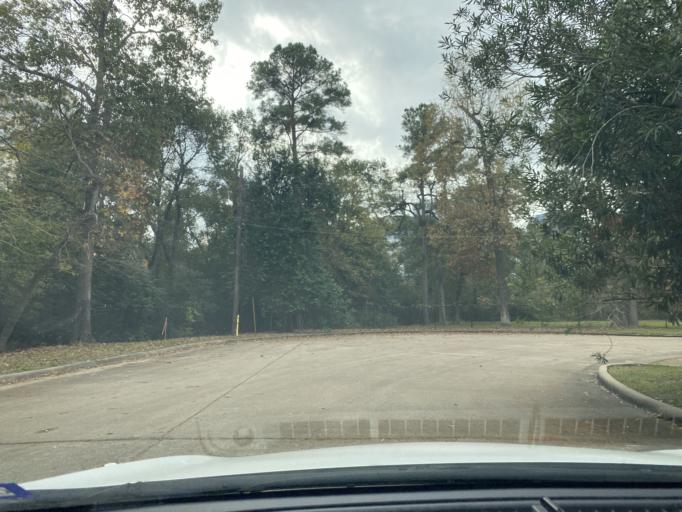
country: US
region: Texas
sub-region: Harris County
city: Hunters Creek Village
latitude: 29.7585
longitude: -95.4599
